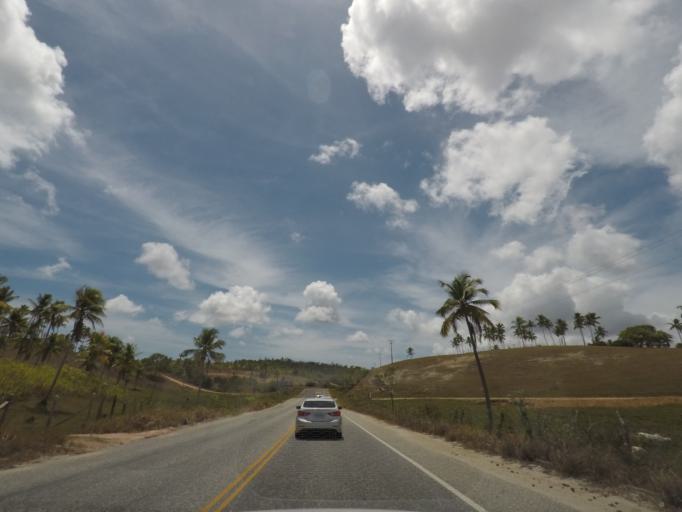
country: BR
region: Sergipe
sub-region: Indiaroba
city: Indiaroba
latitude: -11.4885
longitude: -37.4919
